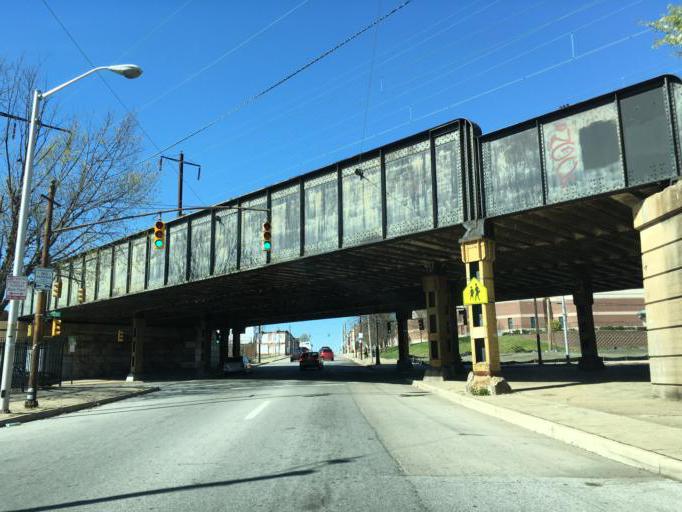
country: US
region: Maryland
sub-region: City of Baltimore
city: Baltimore
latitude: 39.3042
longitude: -76.5900
